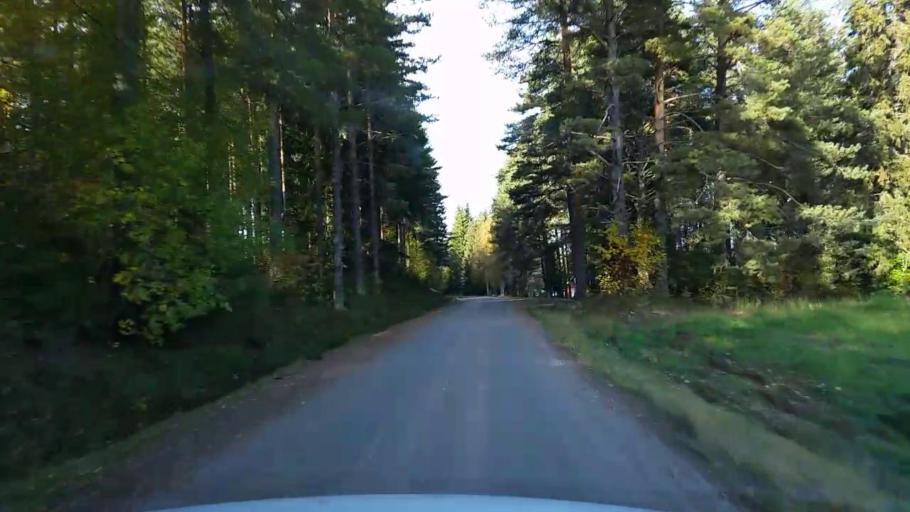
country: SE
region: Gaevleborg
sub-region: Ljusdals Kommun
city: Jaervsoe
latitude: 61.7898
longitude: 16.1858
